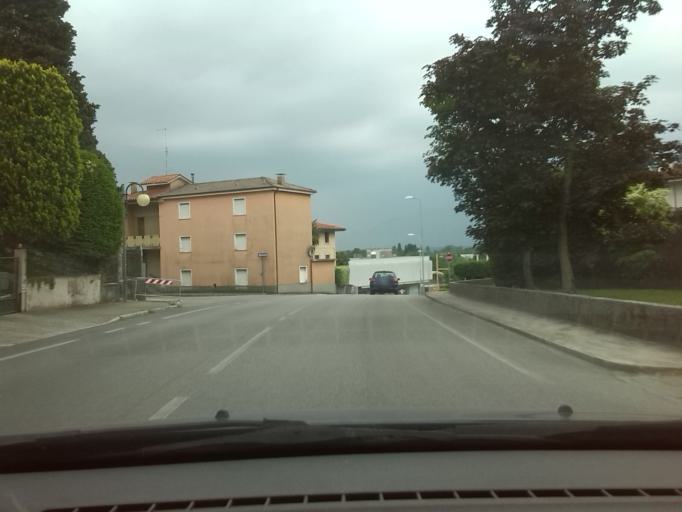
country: IT
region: Friuli Venezia Giulia
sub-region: Provincia di Udine
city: Santo Stefano
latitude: 46.2056
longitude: 13.1242
